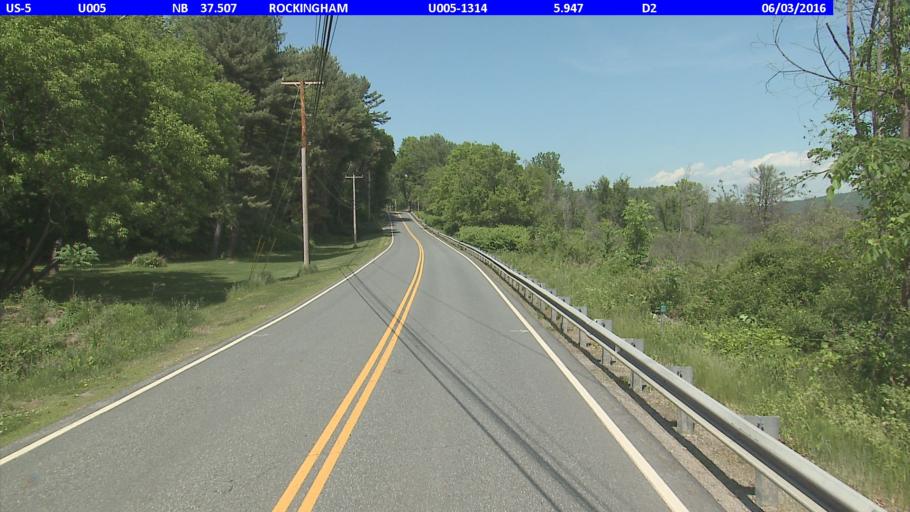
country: US
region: Vermont
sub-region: Windham County
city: Rockingham
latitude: 43.2006
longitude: -72.4512
